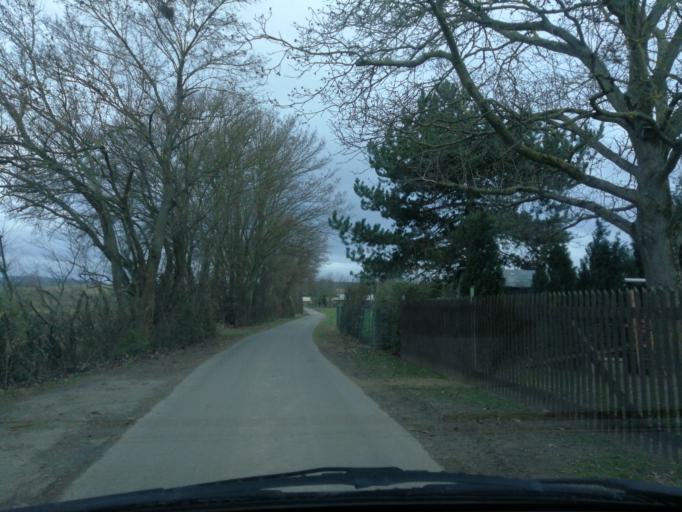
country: DE
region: Hesse
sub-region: Regierungsbezirk Darmstadt
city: Rossdorf
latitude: 49.8395
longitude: 8.7917
